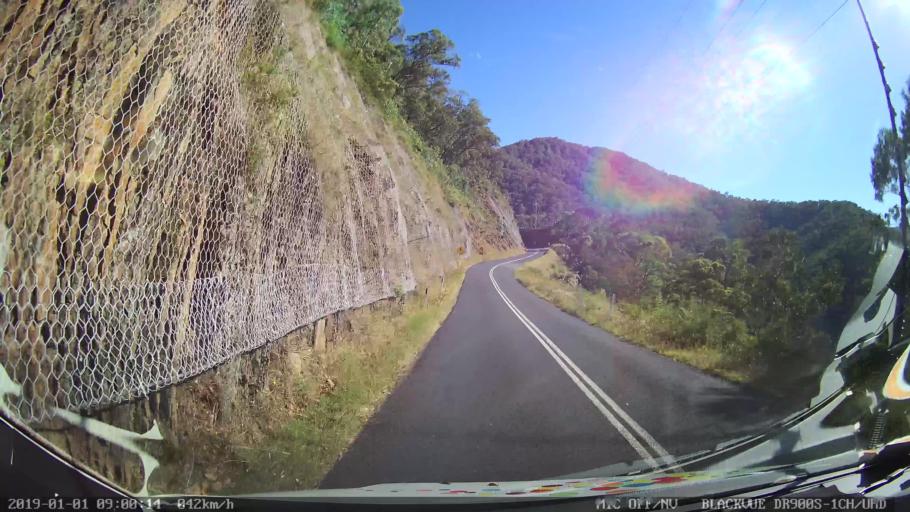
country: AU
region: New South Wales
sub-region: Snowy River
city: Jindabyne
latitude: -36.2366
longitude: 148.1817
